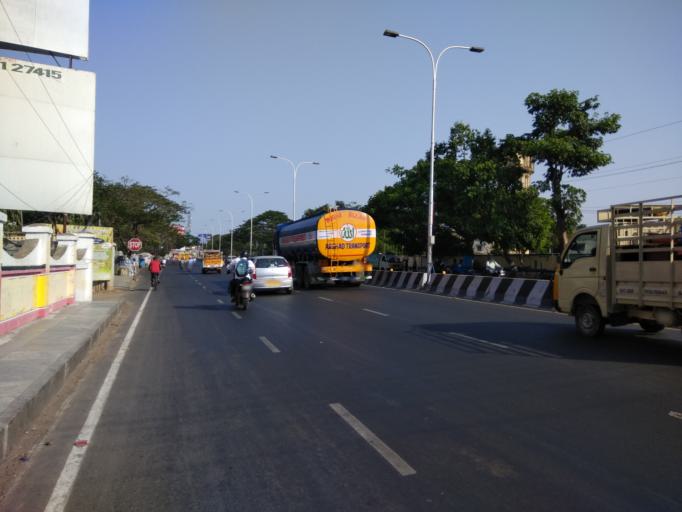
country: IN
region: Tamil Nadu
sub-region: Kancheepuram
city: Saint Thomas Mount
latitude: 13.0132
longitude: 80.1944
